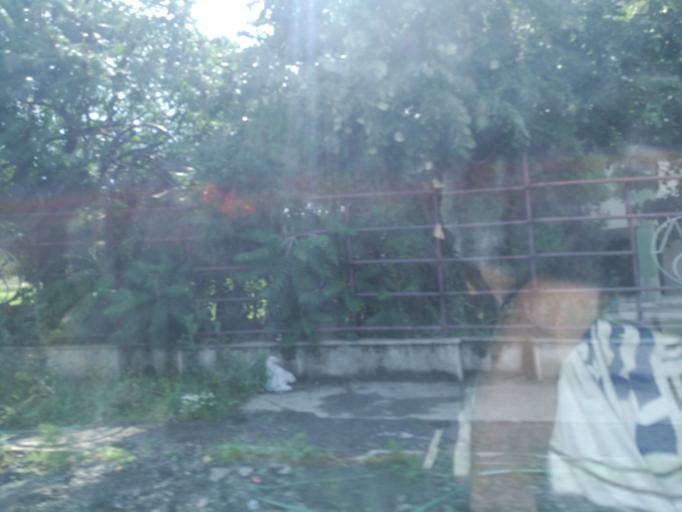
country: RO
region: Constanta
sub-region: Comuna Ovidiu
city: Ovidiu
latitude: 44.2629
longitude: 28.5544
